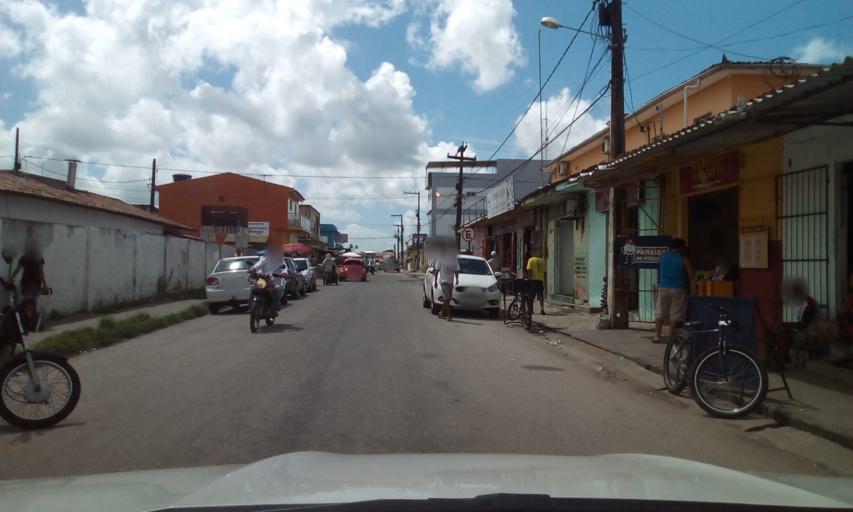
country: BR
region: Paraiba
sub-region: Bayeux
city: Bayeux
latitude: -7.1326
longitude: -34.9276
